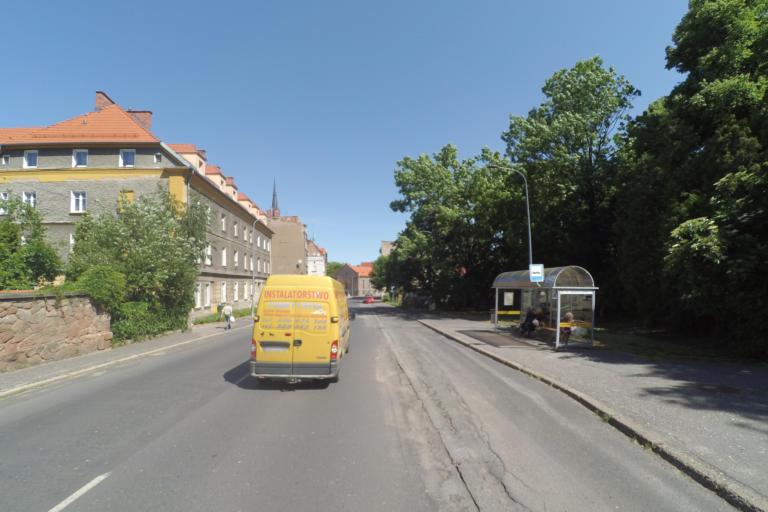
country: PL
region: Lower Silesian Voivodeship
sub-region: Powiat walbrzyski
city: Walbrzych
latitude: 50.7618
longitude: 16.2841
